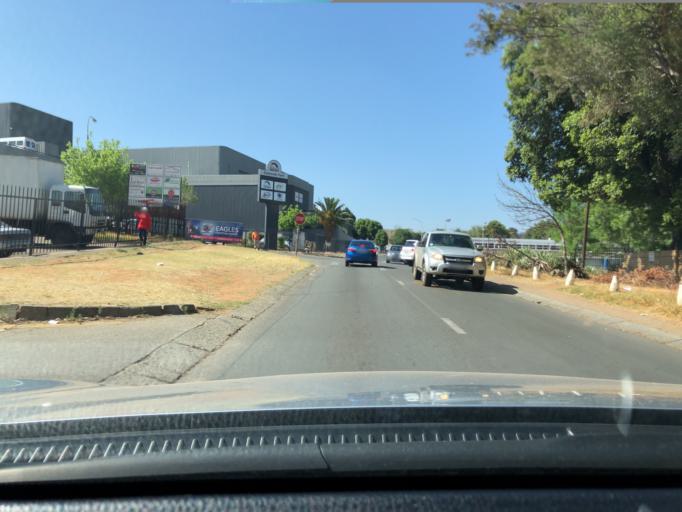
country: ZA
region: Gauteng
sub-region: City of Johannesburg Metropolitan Municipality
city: Modderfontein
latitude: -26.1185
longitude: 28.0829
